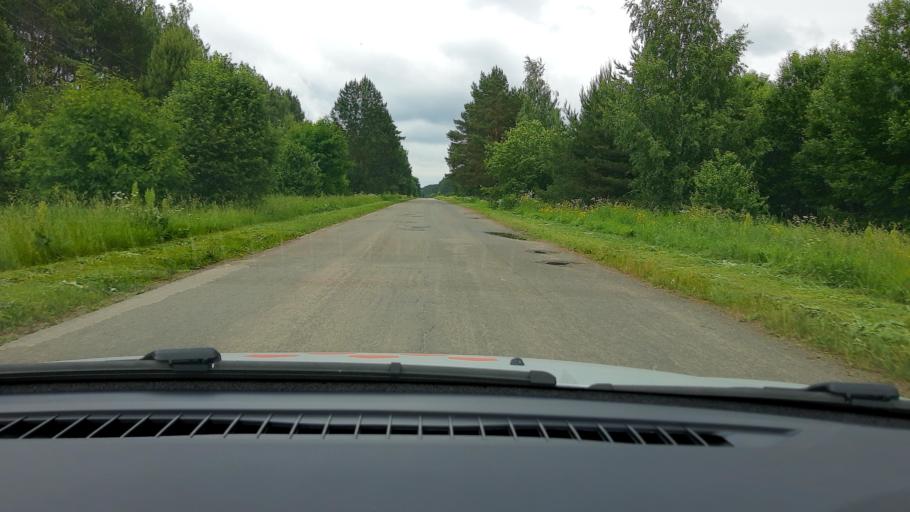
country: RU
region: Nizjnij Novgorod
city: Bogorodsk
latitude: 56.0281
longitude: 43.4599
